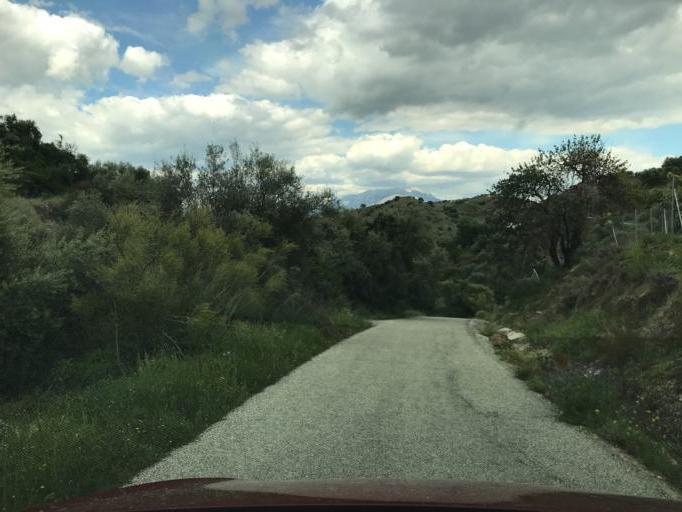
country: ES
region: Andalusia
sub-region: Provincia de Malaga
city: Comares
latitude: 36.8756
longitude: -4.2637
